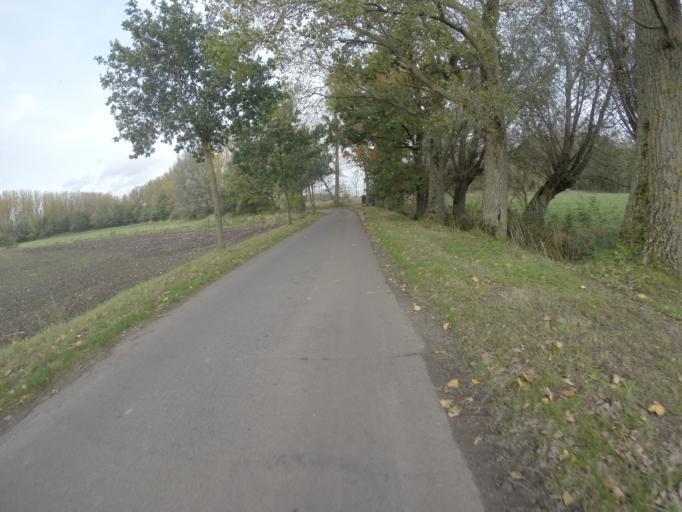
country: BE
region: Flanders
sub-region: Provincie Oost-Vlaanderen
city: Knesselare
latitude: 51.1677
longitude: 3.4264
